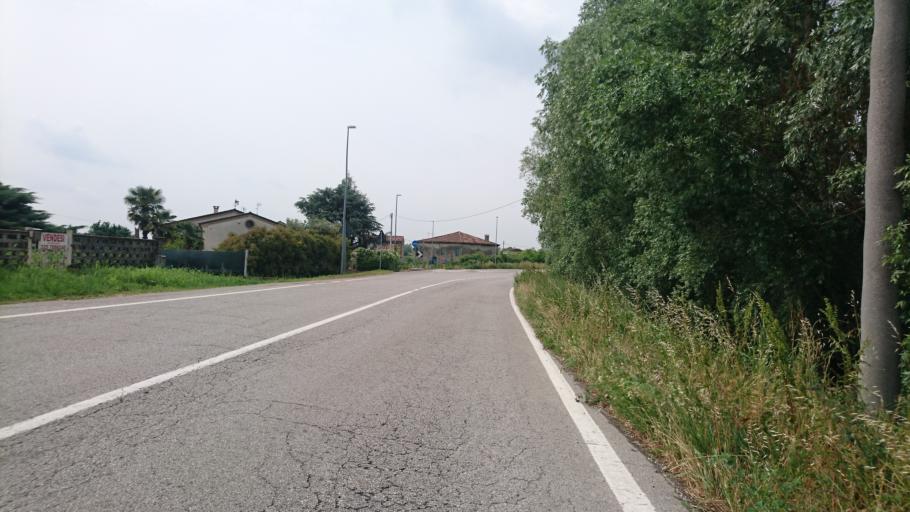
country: IT
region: Veneto
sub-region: Provincia di Padova
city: Vighizzolo d'Este
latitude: 45.1423
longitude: 11.6429
